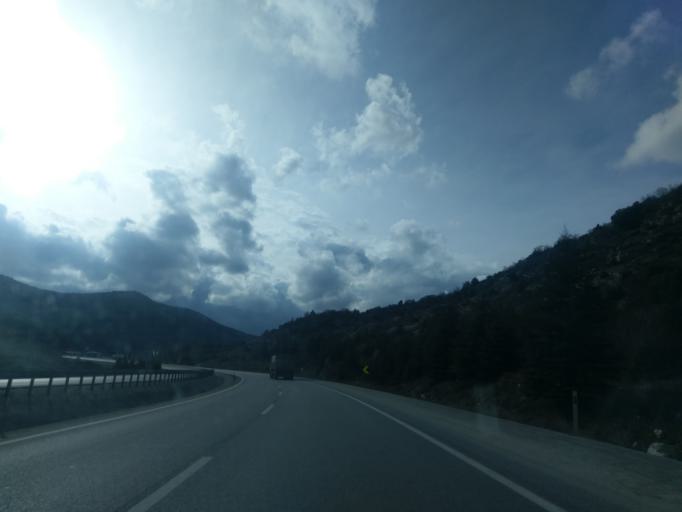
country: TR
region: Kuetahya
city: Sabuncu
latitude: 39.5704
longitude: 30.0756
